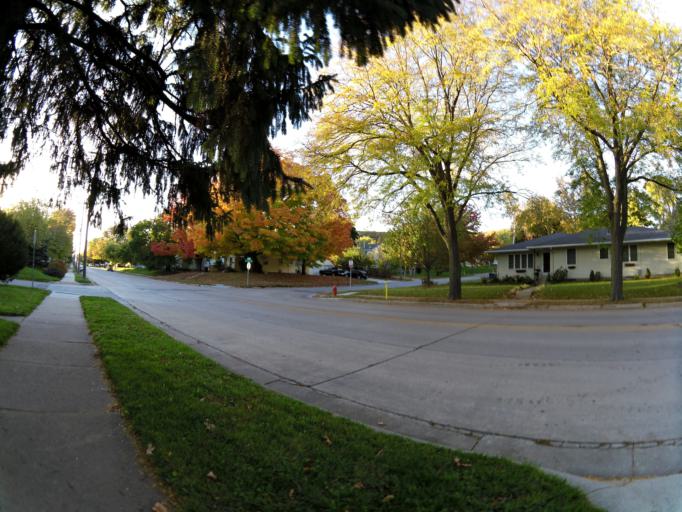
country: US
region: Minnesota
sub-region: Olmsted County
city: Rochester
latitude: 44.0360
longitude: -92.4697
